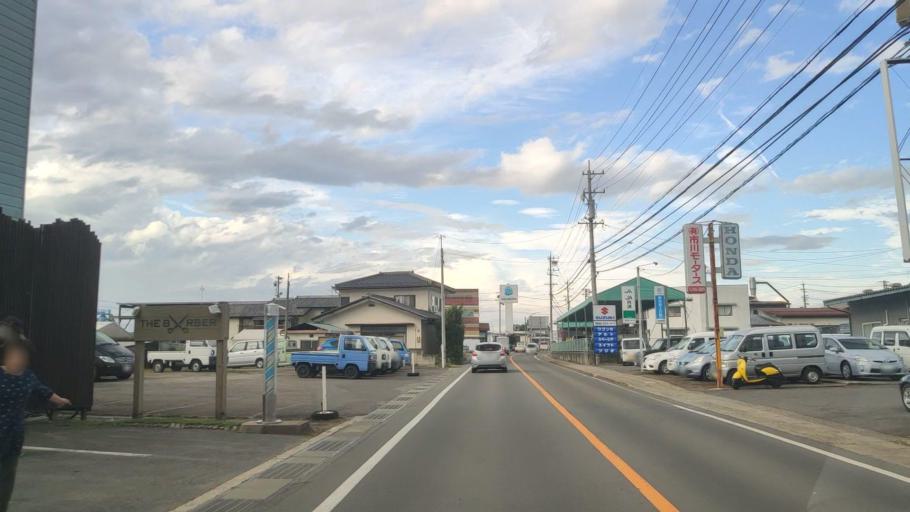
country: JP
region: Nagano
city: Suzaka
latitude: 36.6700
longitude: 138.3158
